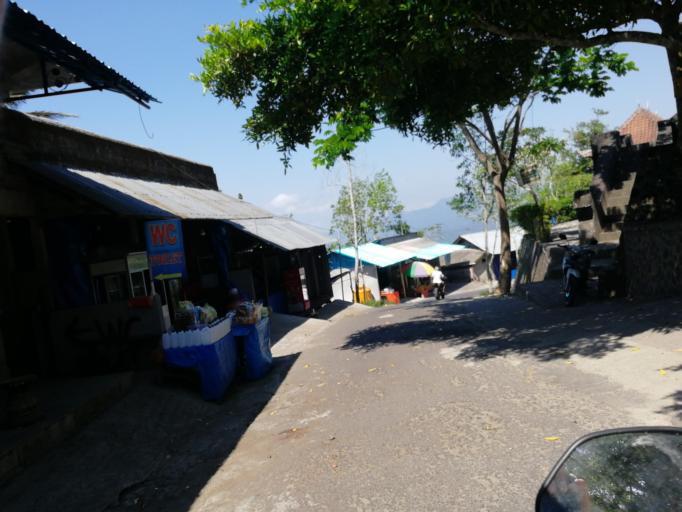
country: ID
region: Bali
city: Tiyingtali Kelod
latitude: -8.3917
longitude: 115.6317
